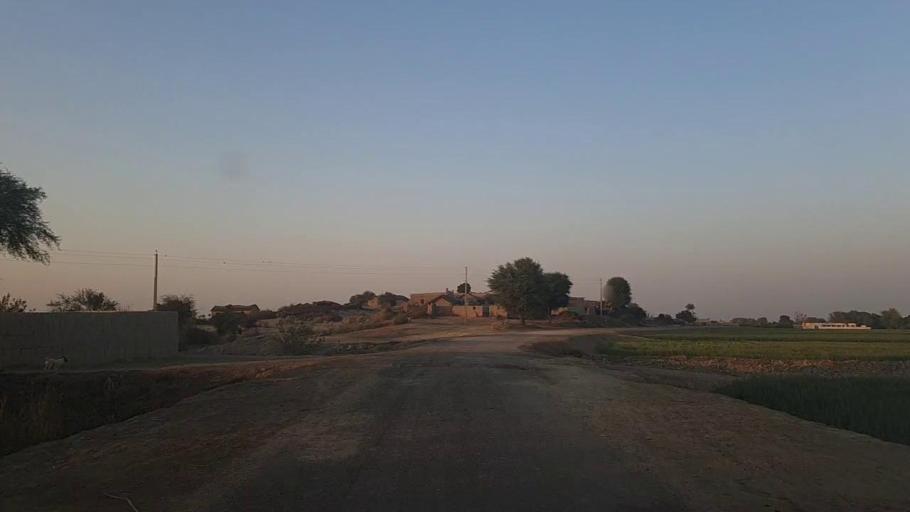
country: PK
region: Sindh
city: Jam Sahib
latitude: 26.3677
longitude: 68.7217
